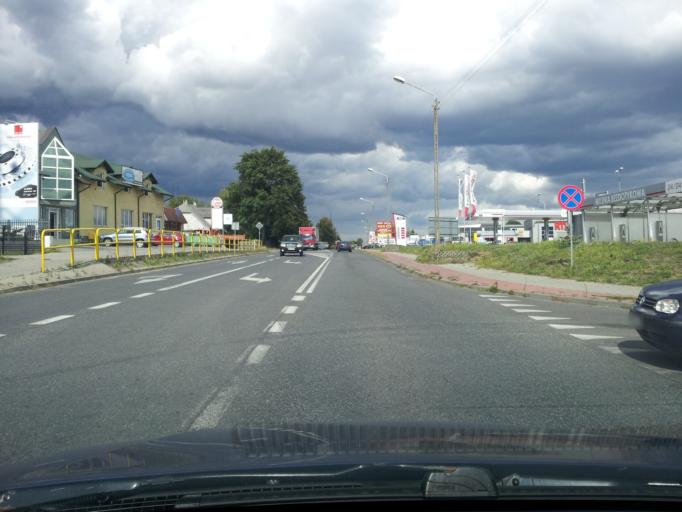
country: PL
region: Kujawsko-Pomorskie
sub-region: Powiat brodnicki
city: Brodnica
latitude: 53.2374
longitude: 19.3920
